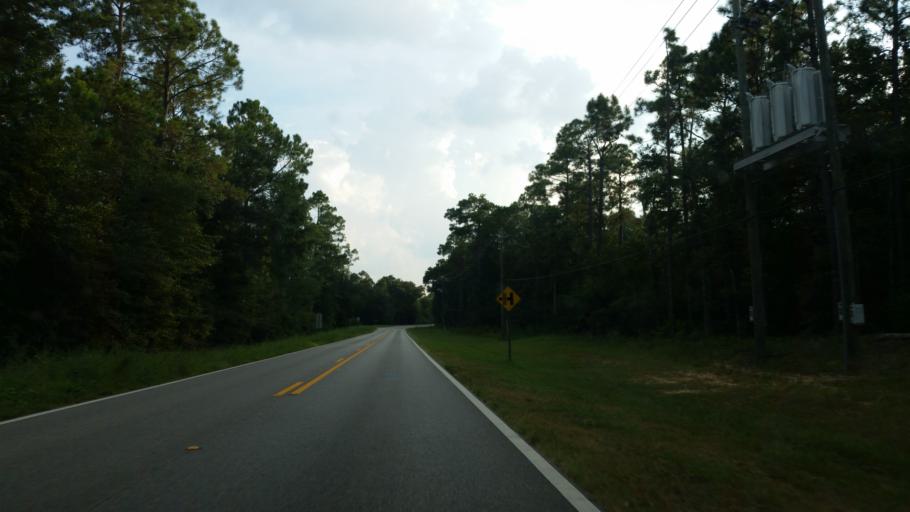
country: US
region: Florida
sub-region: Santa Rosa County
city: Pace
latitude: 30.5628
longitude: -87.1071
